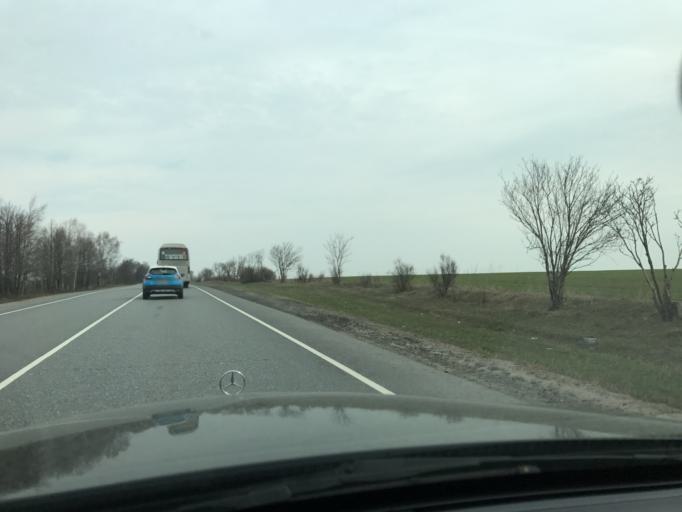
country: RU
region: Vladimir
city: Bogolyubovo
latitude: 56.2901
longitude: 40.4684
